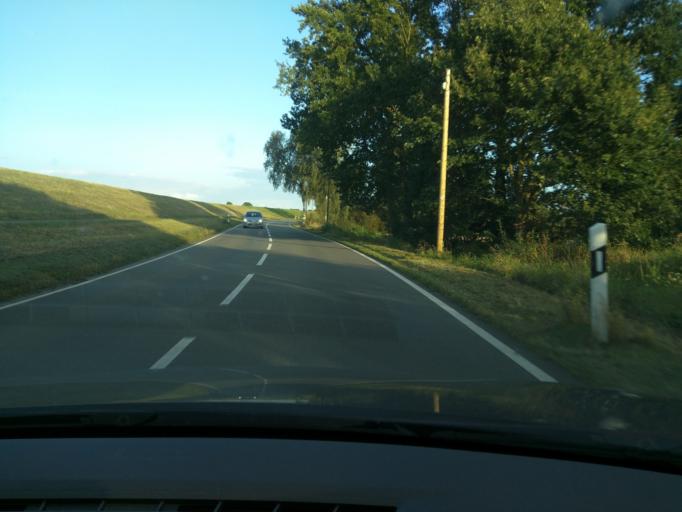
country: DE
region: Lower Saxony
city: Artlenburg
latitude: 53.3778
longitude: 10.4752
